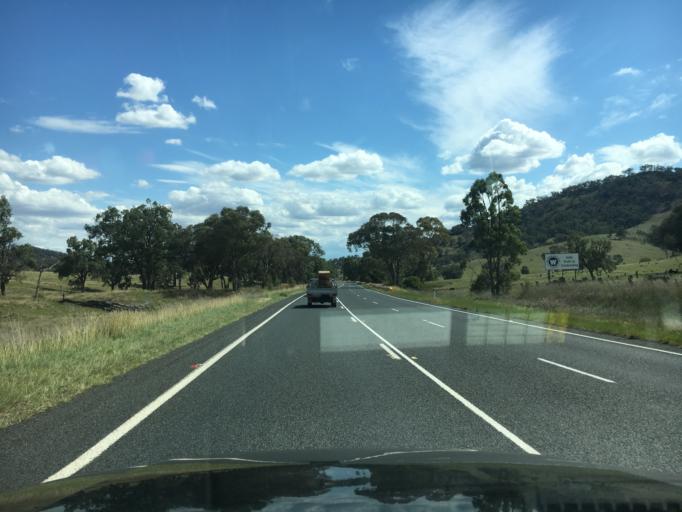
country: AU
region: New South Wales
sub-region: Liverpool Plains
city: Quirindi
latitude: -31.5097
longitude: 150.8584
